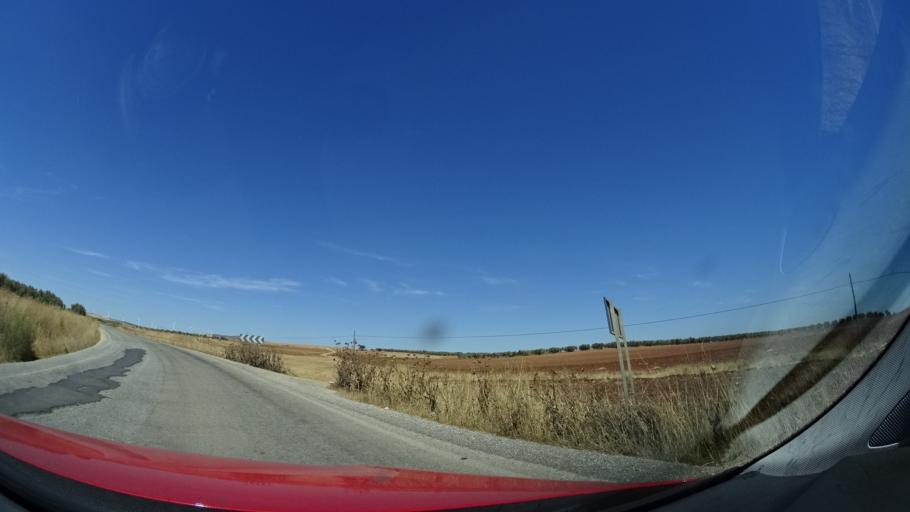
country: ES
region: Andalusia
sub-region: Provincia de Malaga
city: Campillos
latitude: 37.0686
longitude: -4.8611
